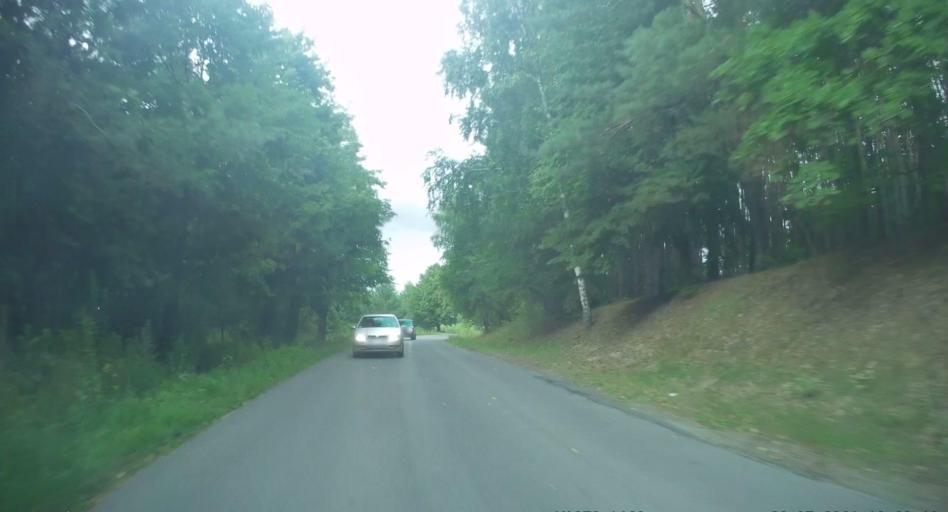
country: PL
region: Lodz Voivodeship
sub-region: Powiat rawski
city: Rawa Mazowiecka
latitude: 51.7444
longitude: 20.2042
